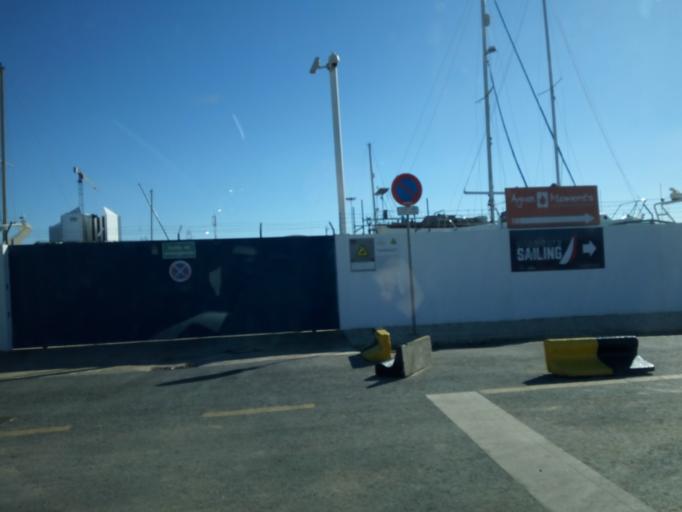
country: PT
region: Faro
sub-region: Loule
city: Vilamoura
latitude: 37.0753
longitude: -8.1252
